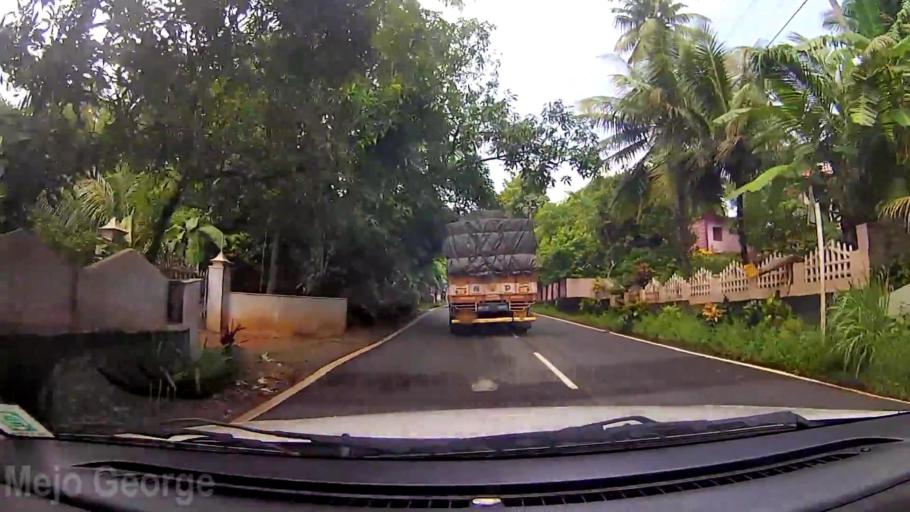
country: IN
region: Kerala
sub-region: Thrissur District
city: Kizhake Chalakudi
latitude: 10.3357
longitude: 76.3039
